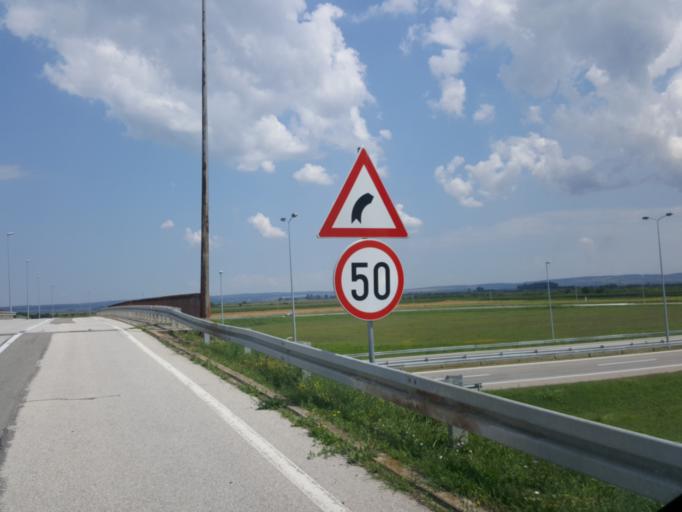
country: RS
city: Ravnje
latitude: 45.0393
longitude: 19.3869
